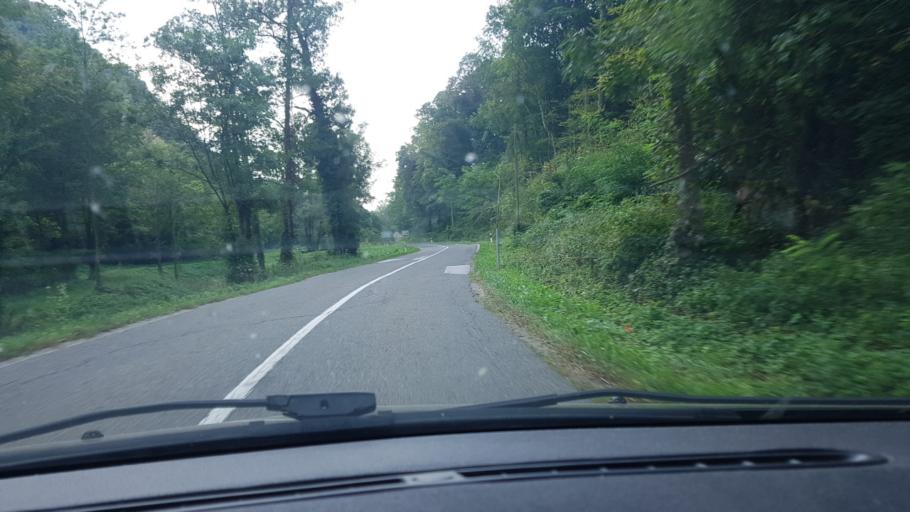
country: HR
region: Krapinsko-Zagorska
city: Mihovljan
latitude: 46.1152
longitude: 16.0086
